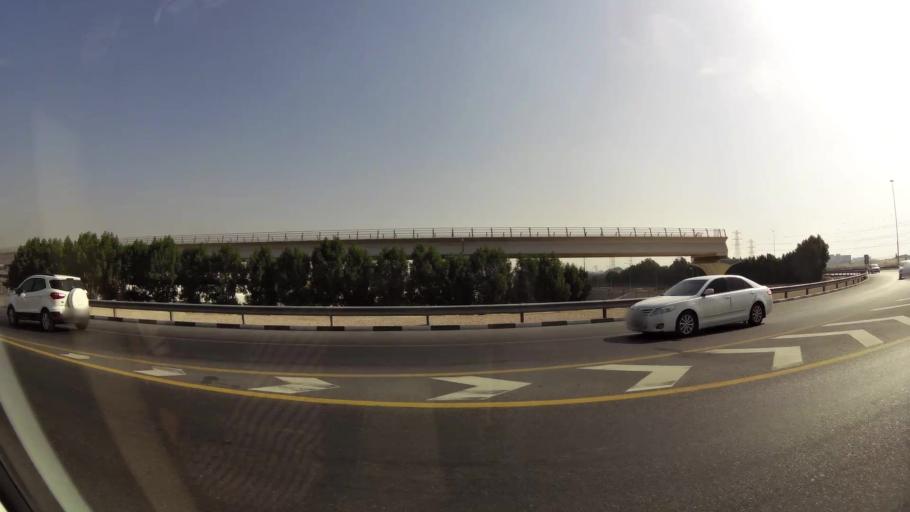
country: AE
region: Ash Shariqah
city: Sharjah
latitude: 25.2527
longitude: 55.4048
